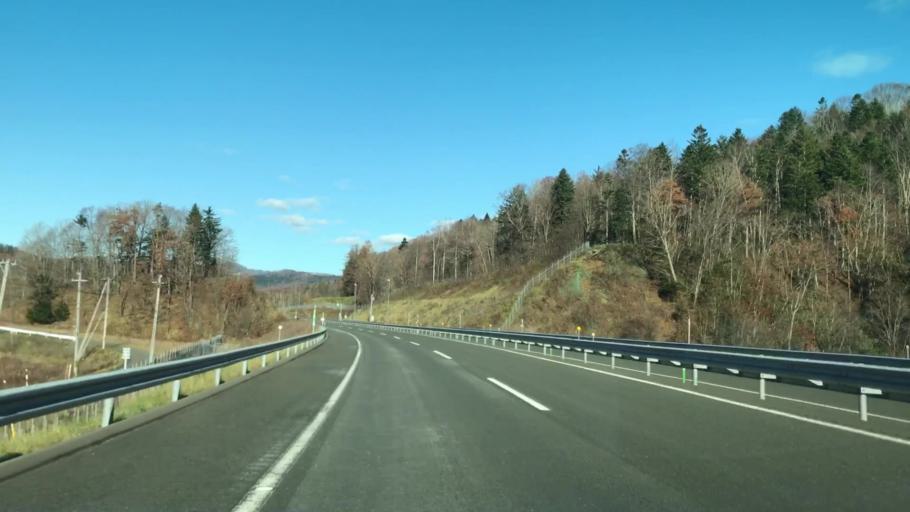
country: JP
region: Hokkaido
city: Shimo-furano
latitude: 42.9236
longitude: 142.2021
